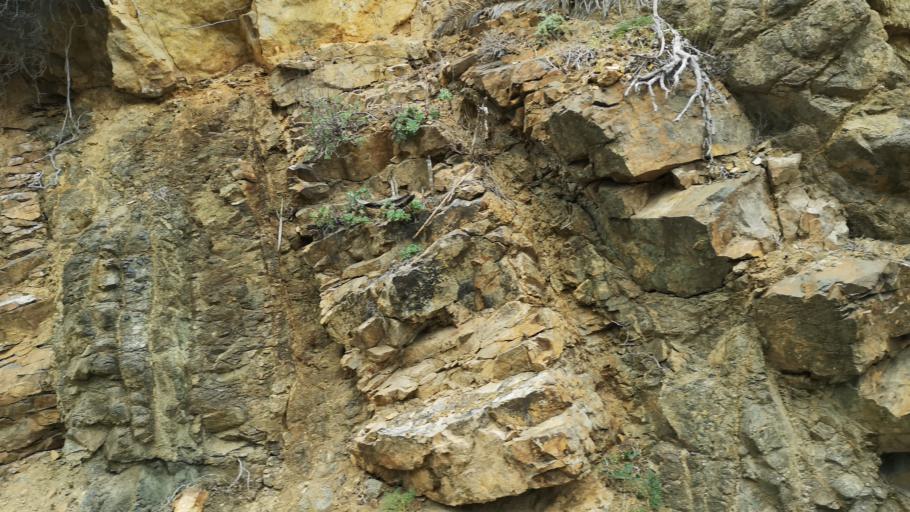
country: ES
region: Canary Islands
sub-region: Provincia de Santa Cruz de Tenerife
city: Vallehermosa
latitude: 28.1890
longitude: -17.2625
